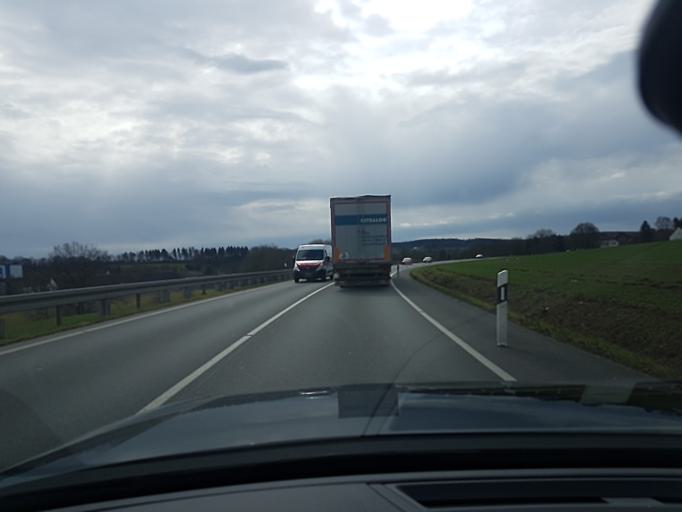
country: DE
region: North Rhine-Westphalia
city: Iserlohn
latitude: 51.4327
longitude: 7.6798
